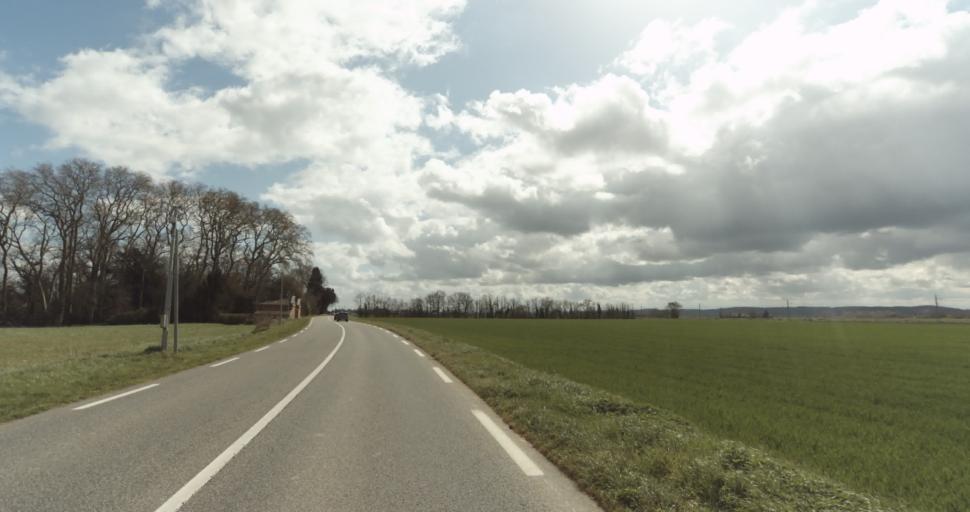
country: FR
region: Midi-Pyrenees
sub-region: Departement de la Haute-Garonne
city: Auterive
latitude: 43.3325
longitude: 1.4870
